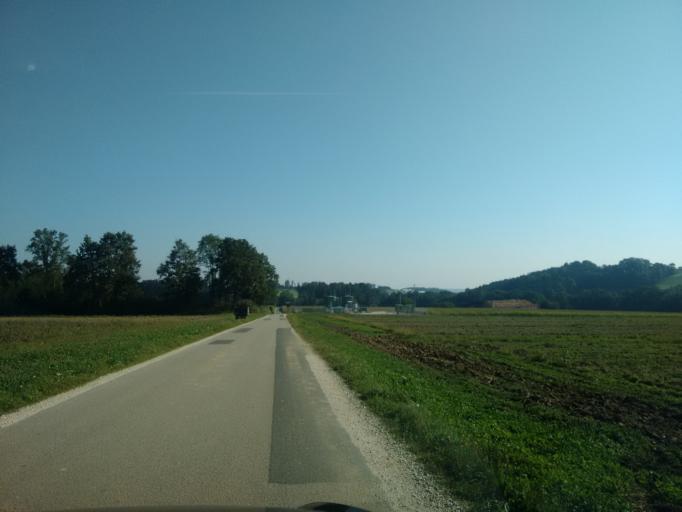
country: AT
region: Upper Austria
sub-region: Wels-Land
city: Marchtrenk
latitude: 48.1335
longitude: 14.1924
